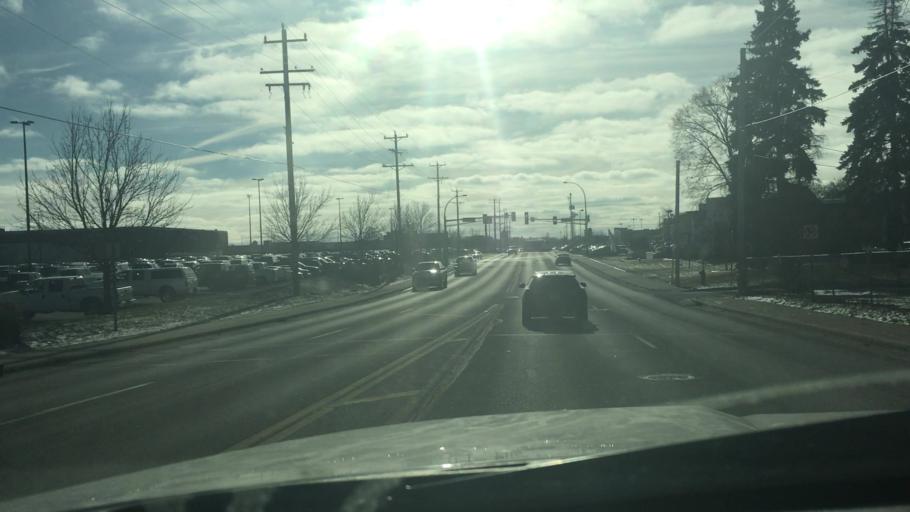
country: US
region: Minnesota
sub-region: Stearns County
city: Waite Park
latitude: 45.5574
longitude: -94.2138
